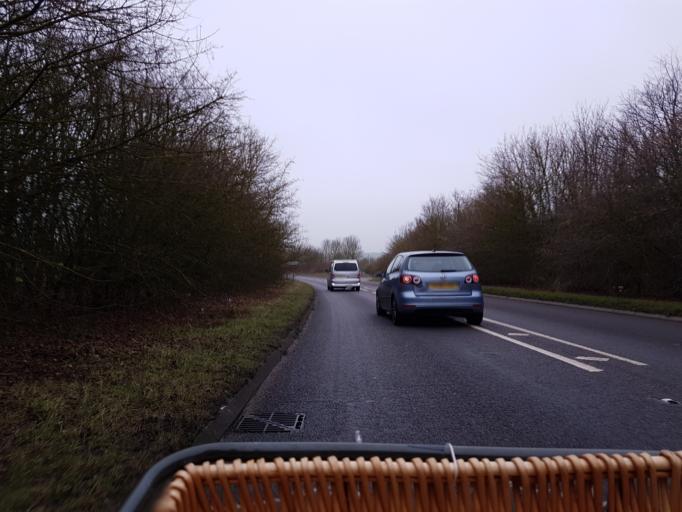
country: GB
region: England
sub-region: Cambridgeshire
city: Duxford
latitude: 52.0719
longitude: 0.1923
